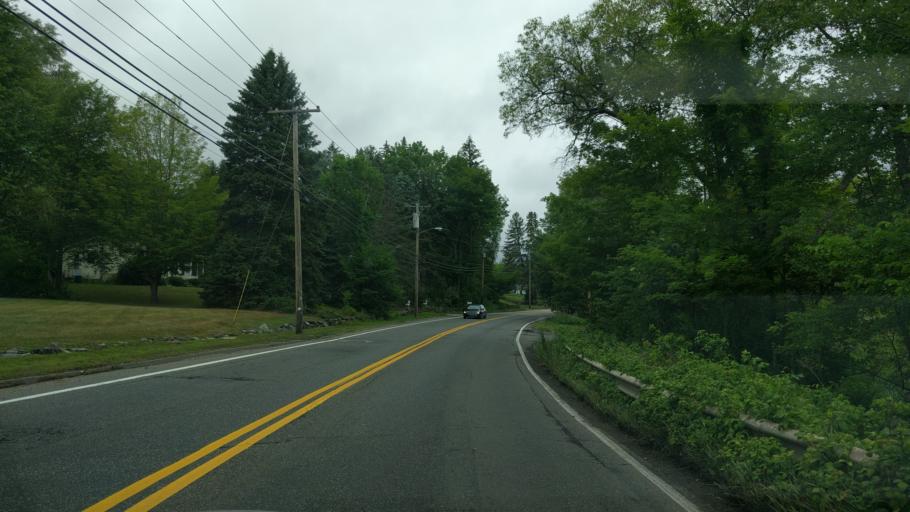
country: US
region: Massachusetts
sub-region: Worcester County
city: Grafton
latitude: 42.2221
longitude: -71.7023
